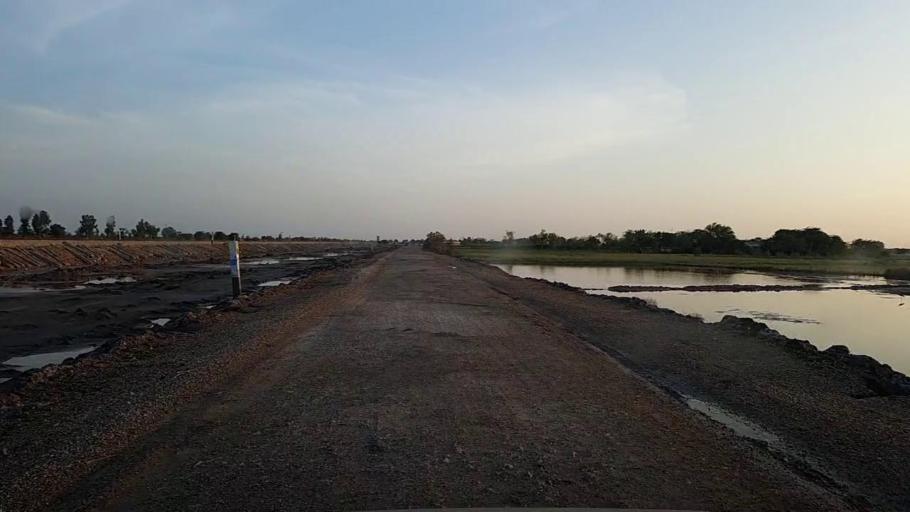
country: PK
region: Sindh
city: Hingorja
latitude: 27.0554
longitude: 68.3899
